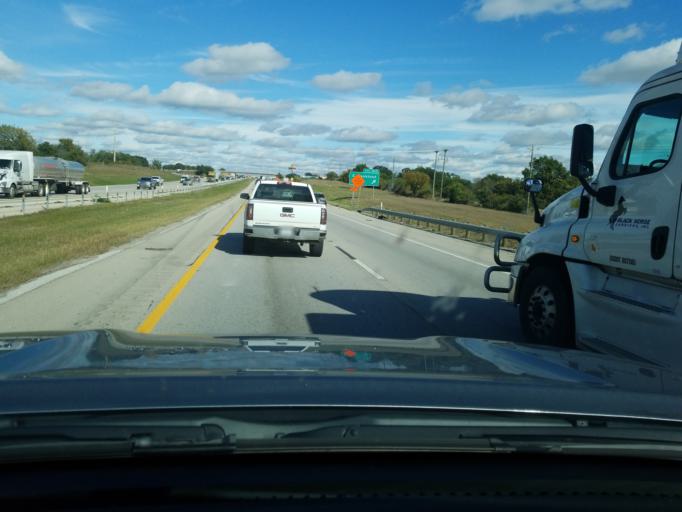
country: US
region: Texas
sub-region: Parker County
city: Hudson Oaks
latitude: 32.7411
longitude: -97.7517
